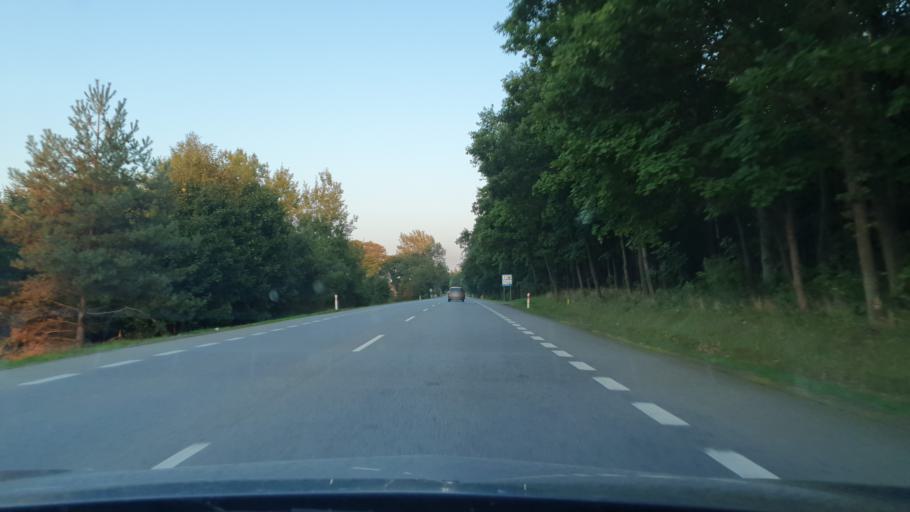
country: PL
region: Pomeranian Voivodeship
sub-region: Powiat leborski
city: Nowa Wies Leborska
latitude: 54.5242
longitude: 17.7041
